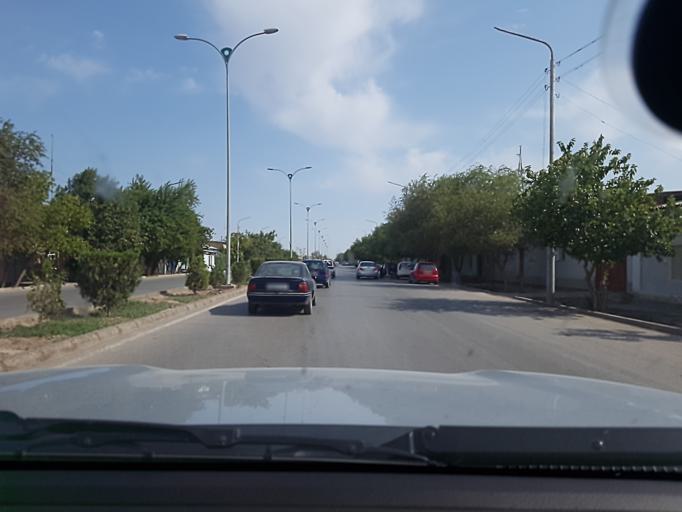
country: TM
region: Dasoguz
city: Dasoguz
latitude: 41.8345
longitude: 59.9816
